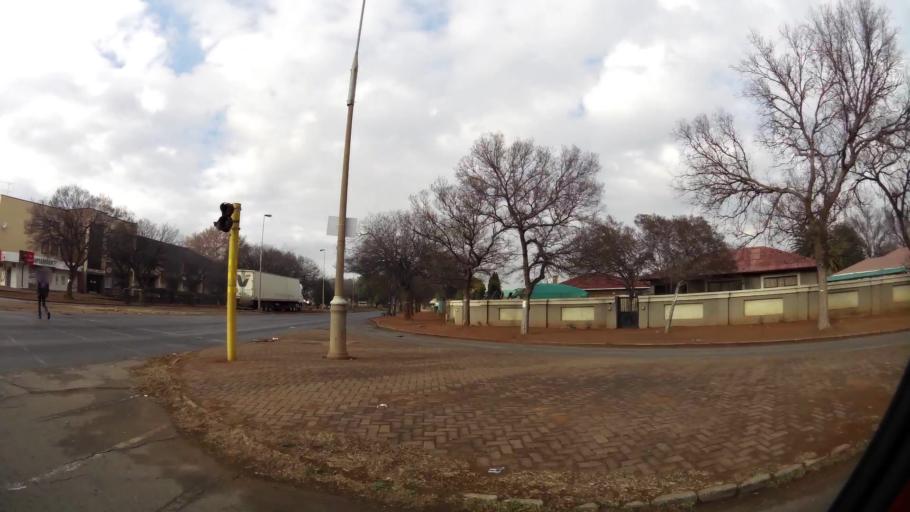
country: ZA
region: Gauteng
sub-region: Sedibeng District Municipality
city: Vanderbijlpark
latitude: -26.6978
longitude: 27.8223
